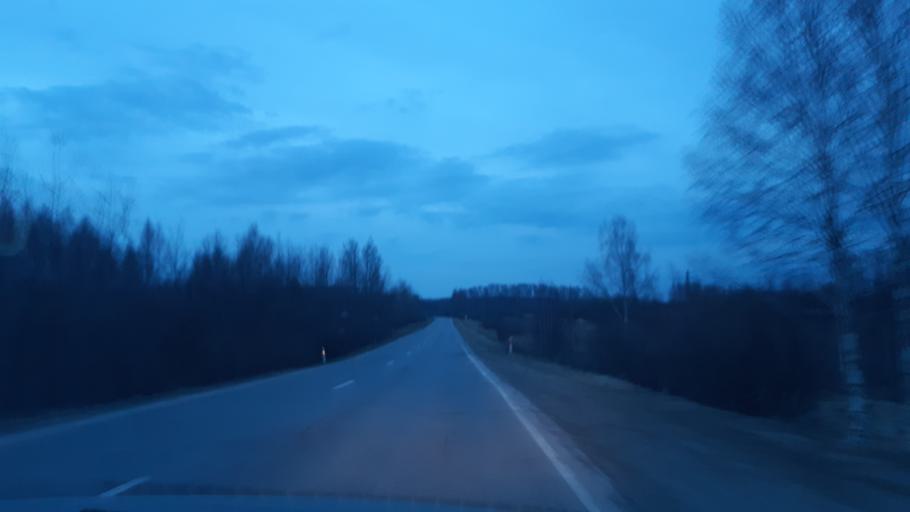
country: RU
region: Vladimir
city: Luknovo
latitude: 56.2174
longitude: 42.0314
